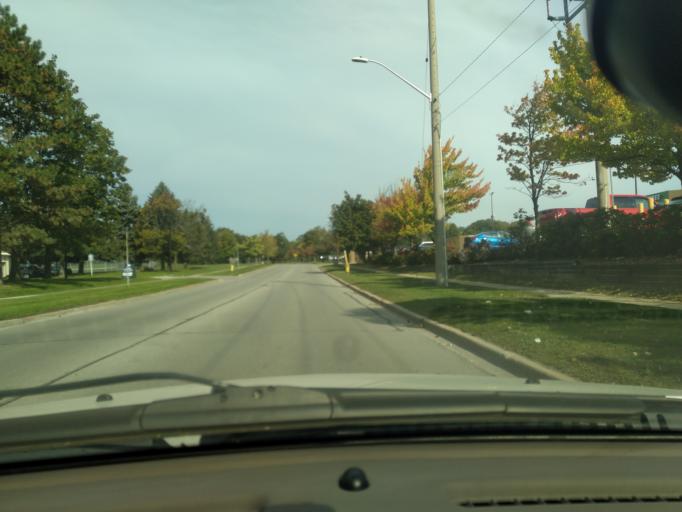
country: CA
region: Ontario
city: Barrie
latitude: 44.4051
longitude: -79.7070
